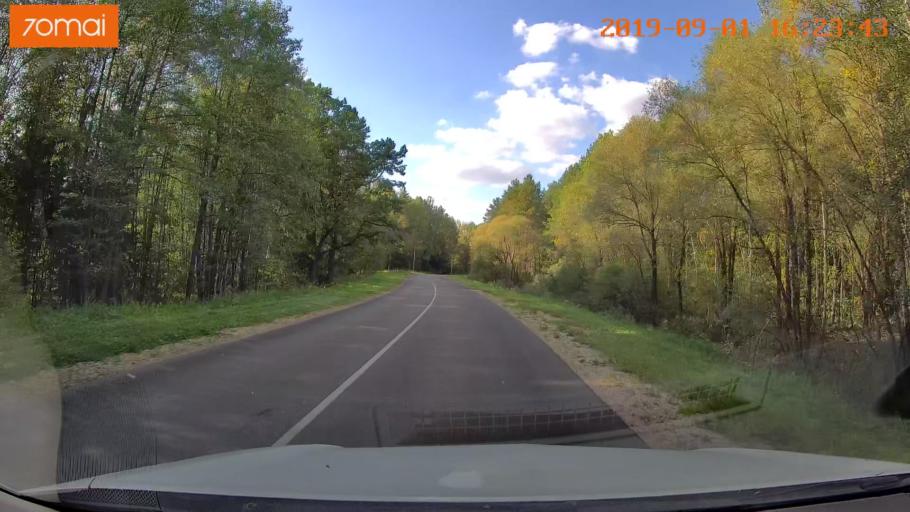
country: RU
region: Kaluga
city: Maloyaroslavets
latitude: 54.8839
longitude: 36.5307
